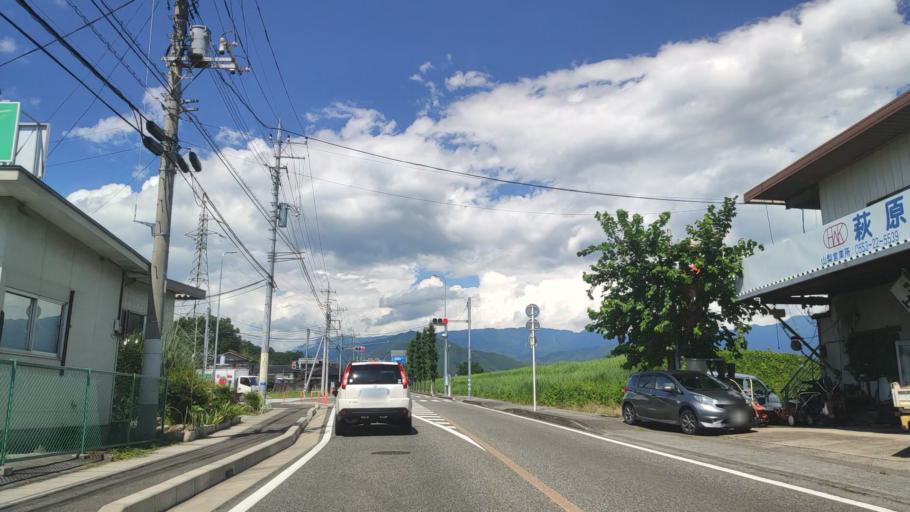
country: JP
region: Yamanashi
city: Enzan
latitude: 35.7010
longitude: 138.6906
